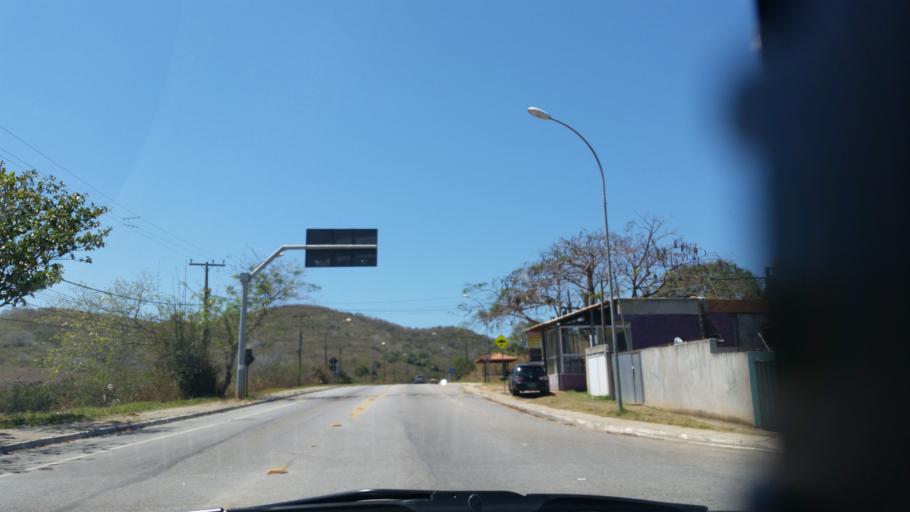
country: BR
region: Rio de Janeiro
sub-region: Armacao De Buzios
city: Armacao de Buzios
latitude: -22.7857
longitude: -41.9535
